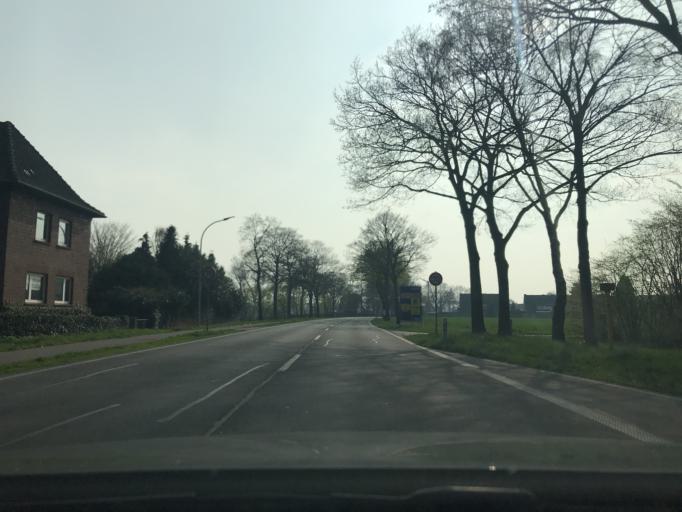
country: DE
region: North Rhine-Westphalia
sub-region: Regierungsbezirk Dusseldorf
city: Goch
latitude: 51.6827
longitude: 6.1785
